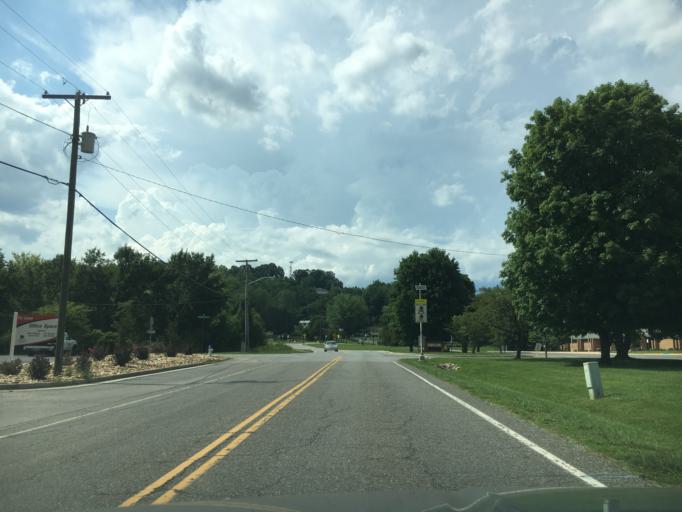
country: US
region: Virginia
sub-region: Roanoke County
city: Cave Spring
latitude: 37.2024
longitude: -79.9996
